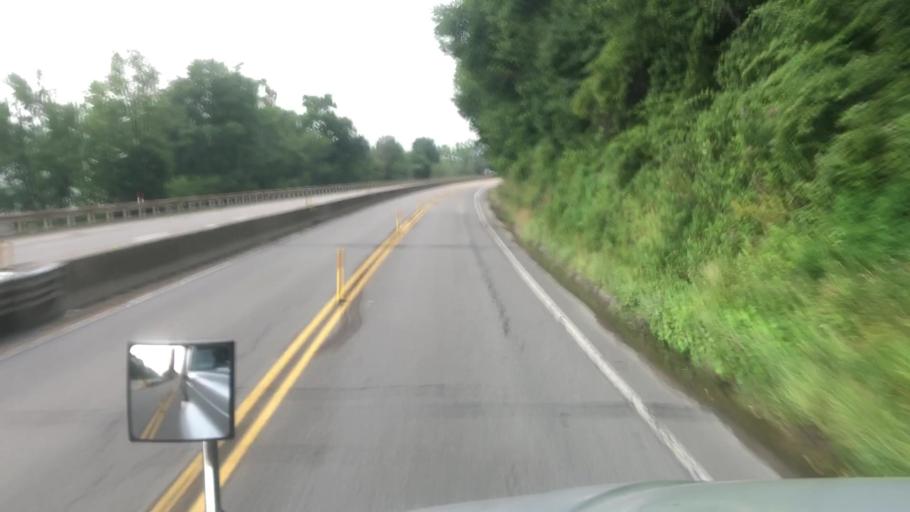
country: US
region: Pennsylvania
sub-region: Venango County
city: Woodland Heights
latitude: 41.4141
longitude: -79.7331
